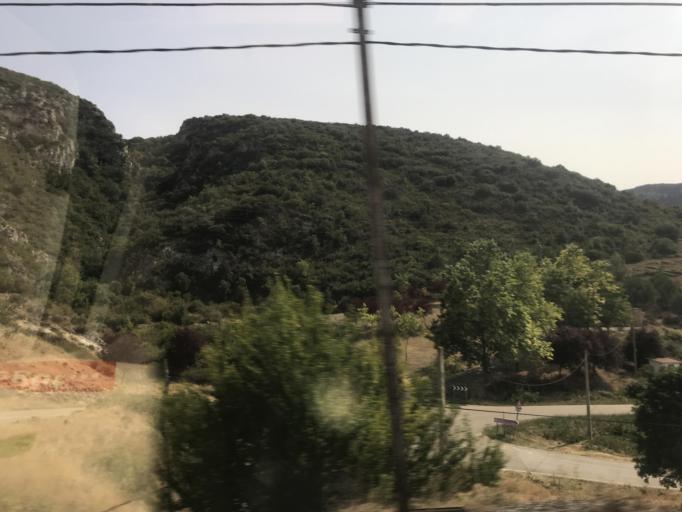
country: ES
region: Castille and Leon
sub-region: Provincia de Burgos
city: Bugedo
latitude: 42.6469
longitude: -3.0207
